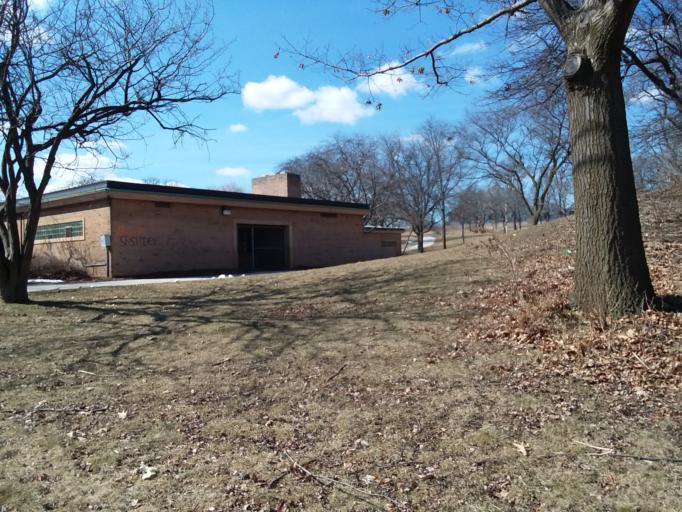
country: US
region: Wisconsin
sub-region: Milwaukee County
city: West Milwaukee
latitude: 43.0265
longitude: -87.9422
